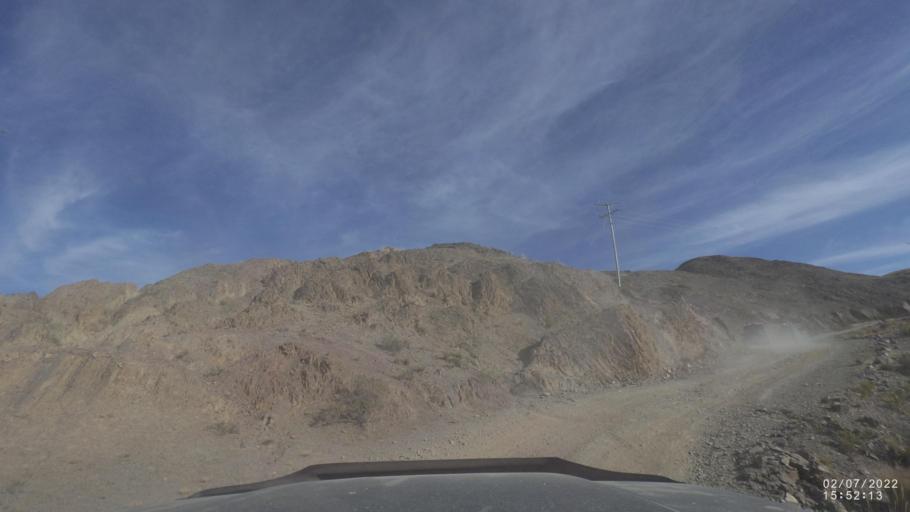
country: BO
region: Cochabamba
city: Irpa Irpa
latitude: -17.9068
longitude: -66.4137
